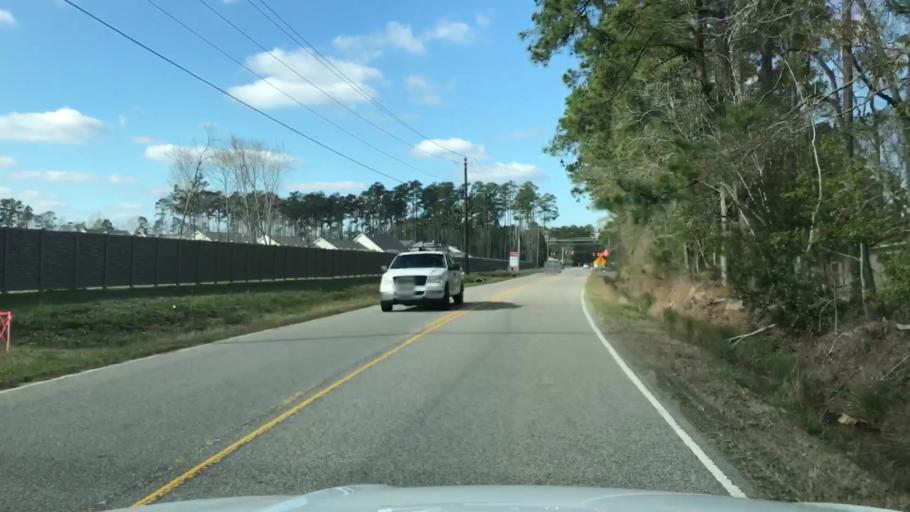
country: US
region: South Carolina
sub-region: Horry County
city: Socastee
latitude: 33.6595
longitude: -79.0082
